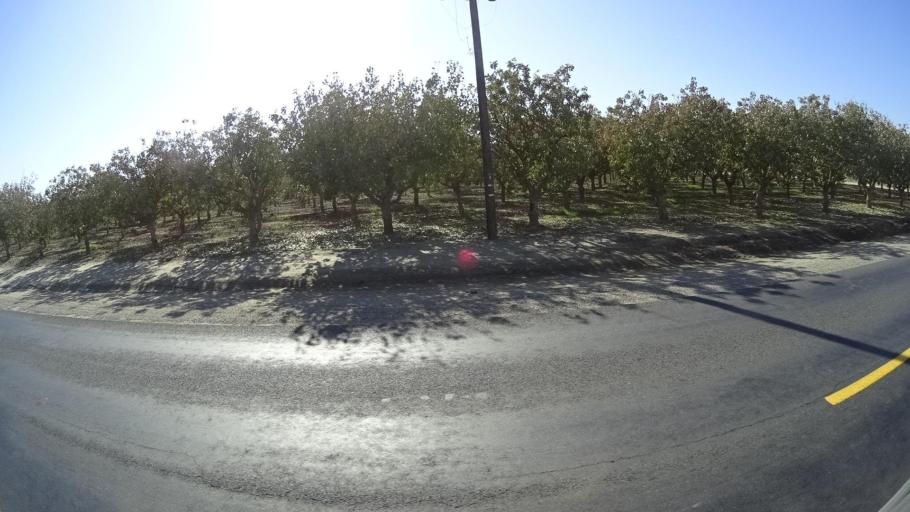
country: US
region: California
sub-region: Kern County
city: Delano
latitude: 35.7177
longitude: -119.3474
